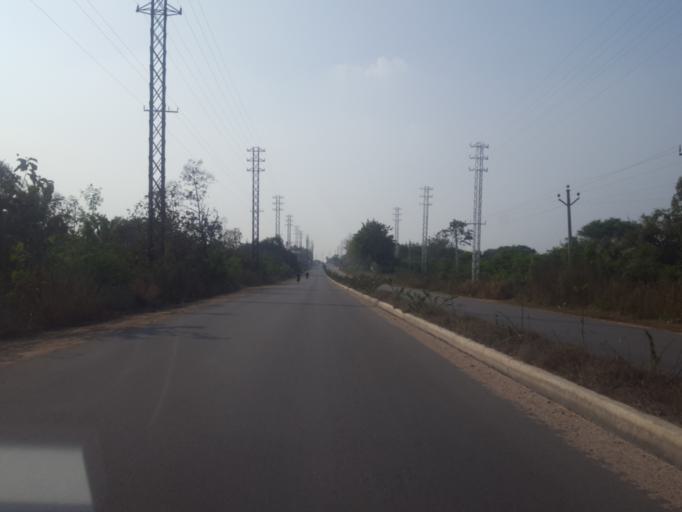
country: IN
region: Telangana
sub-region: Medak
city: Serilingampalle
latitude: 17.4169
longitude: 78.2548
